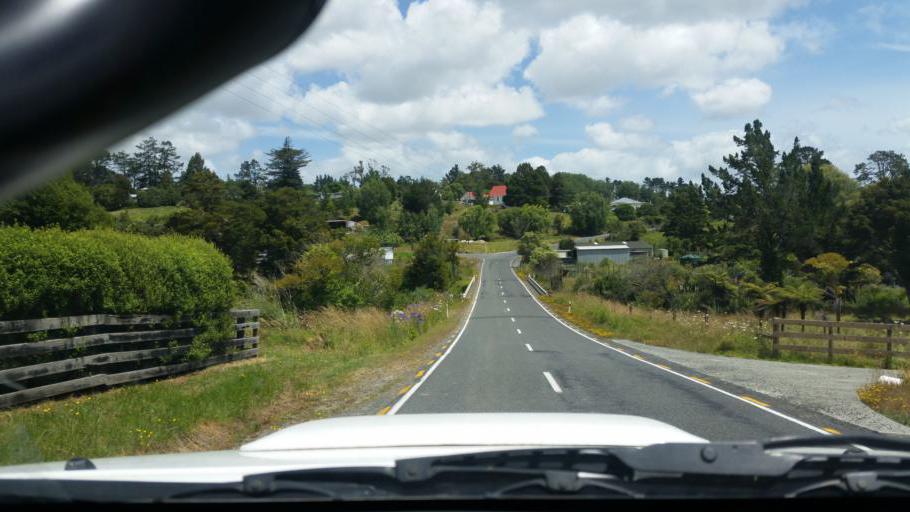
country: NZ
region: Northland
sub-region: Whangarei
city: Ruakaka
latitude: -36.0941
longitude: 174.2432
